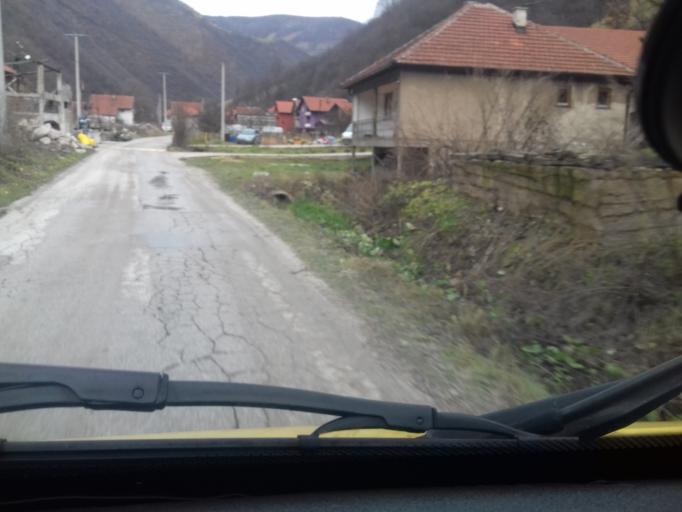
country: BA
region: Federation of Bosnia and Herzegovina
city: Zenica
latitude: 44.2467
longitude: 17.9202
